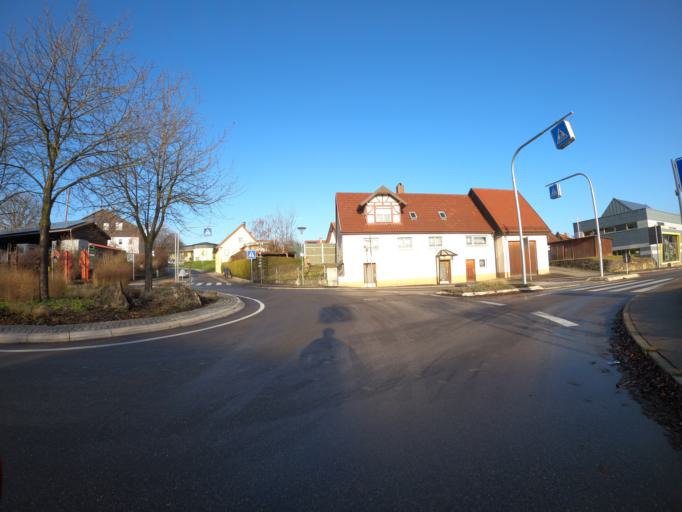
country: DE
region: Baden-Wuerttemberg
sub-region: Regierungsbezirk Stuttgart
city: Hattenhofen
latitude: 48.6663
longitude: 9.5749
